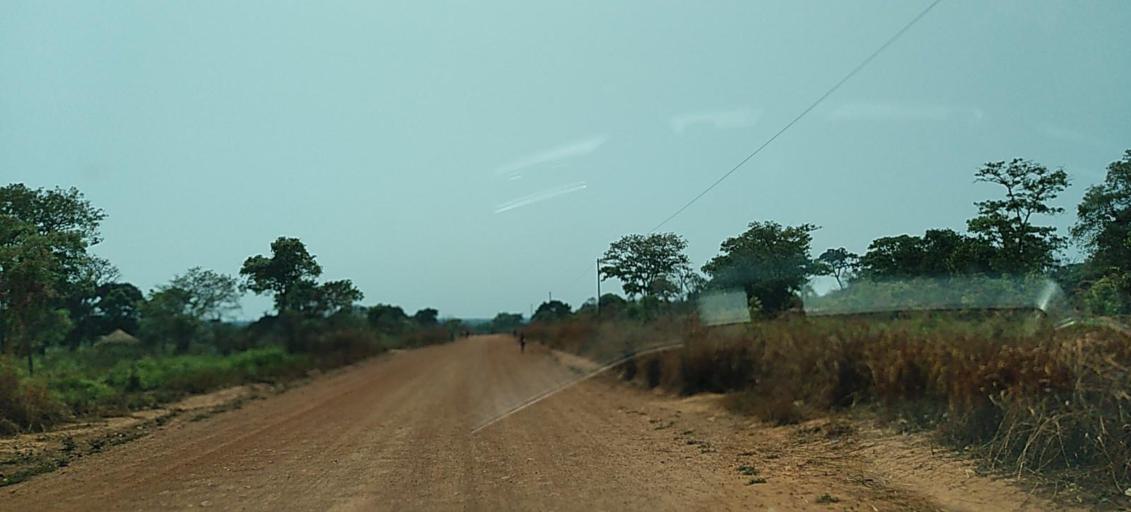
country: ZM
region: North-Western
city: Kansanshi
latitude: -11.9973
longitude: 26.6091
